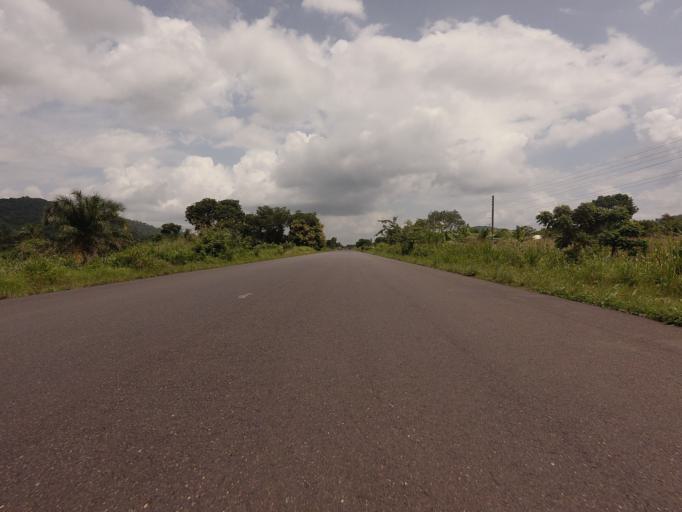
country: GH
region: Volta
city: Ho
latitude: 6.5074
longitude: 0.2116
